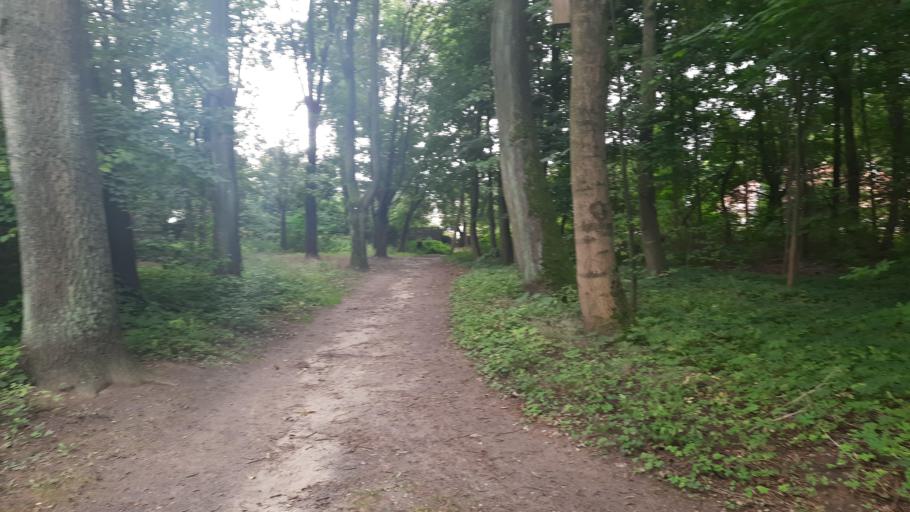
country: PL
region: Lodz Voivodeship
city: Lodz
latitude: 51.8062
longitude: 19.4500
